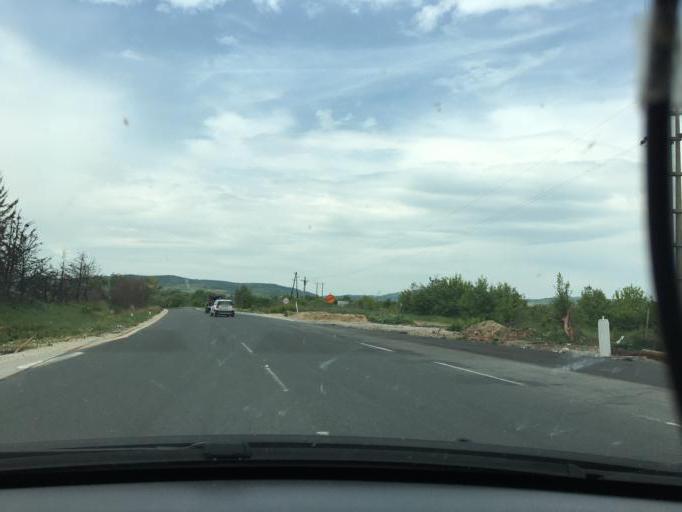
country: MK
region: Veles
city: Veles
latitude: 41.7788
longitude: 21.7672
